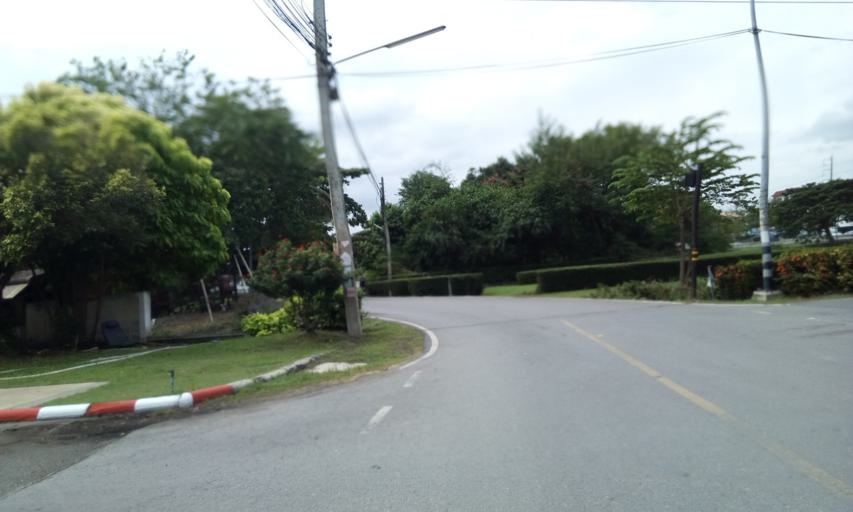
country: TH
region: Pathum Thani
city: Ban Rangsit
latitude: 14.0534
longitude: 100.8292
